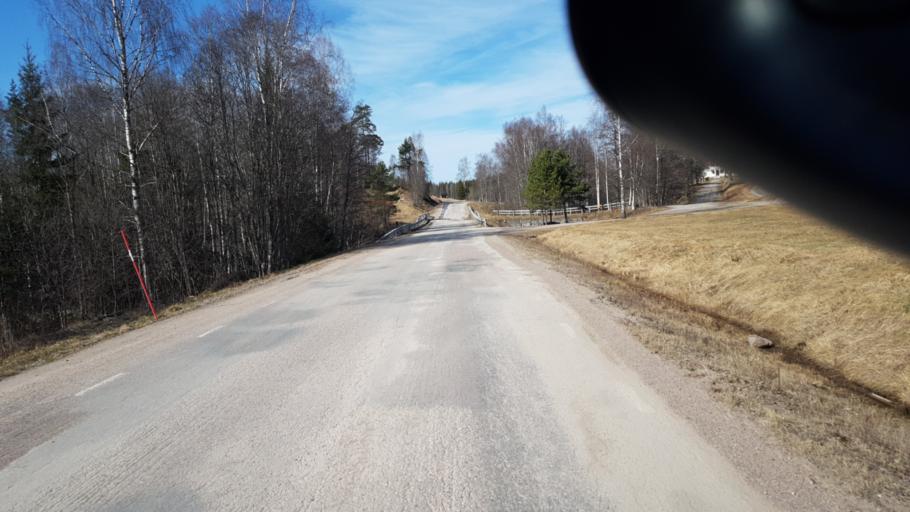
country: SE
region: Vaermland
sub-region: Sunne Kommun
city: Sunne
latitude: 59.6794
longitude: 12.8977
